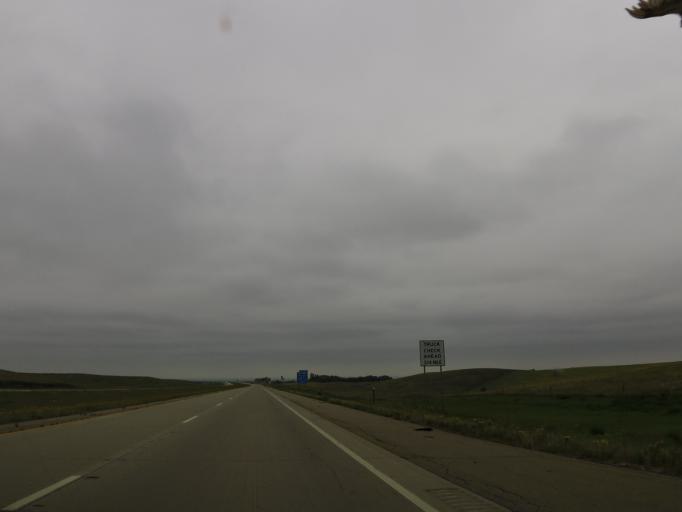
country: US
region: South Dakota
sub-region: Roberts County
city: Sisseton
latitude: 45.3894
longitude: -97.0346
